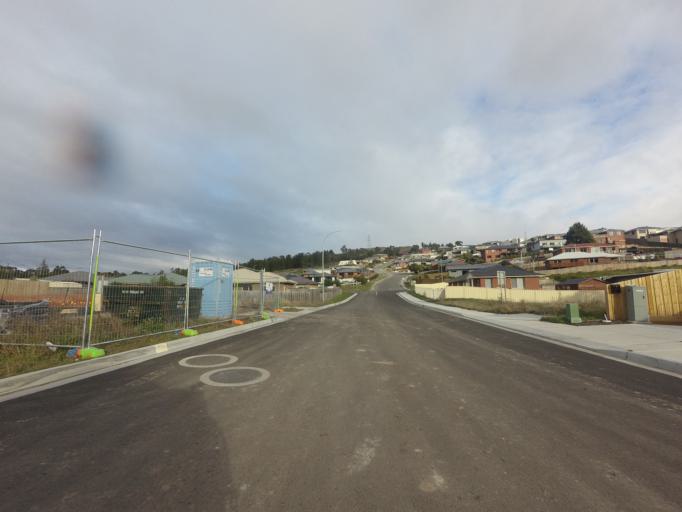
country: AU
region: Tasmania
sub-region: Clarence
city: Warrane
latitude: -42.8569
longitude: 147.4105
